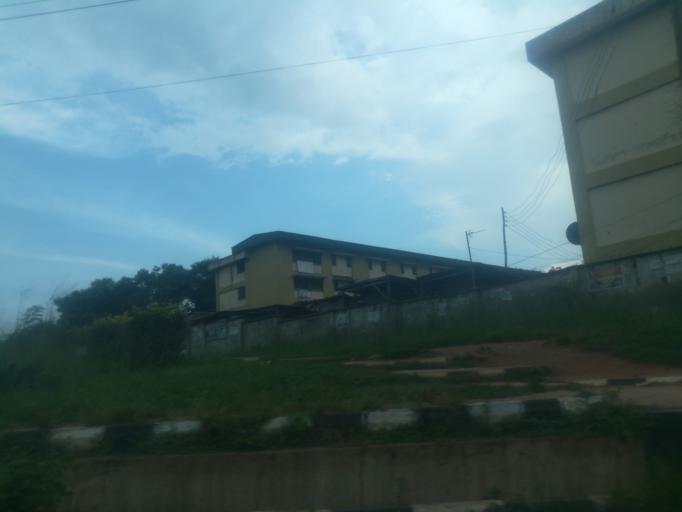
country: NG
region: Oyo
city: Ibadan
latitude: 7.4302
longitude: 3.8931
